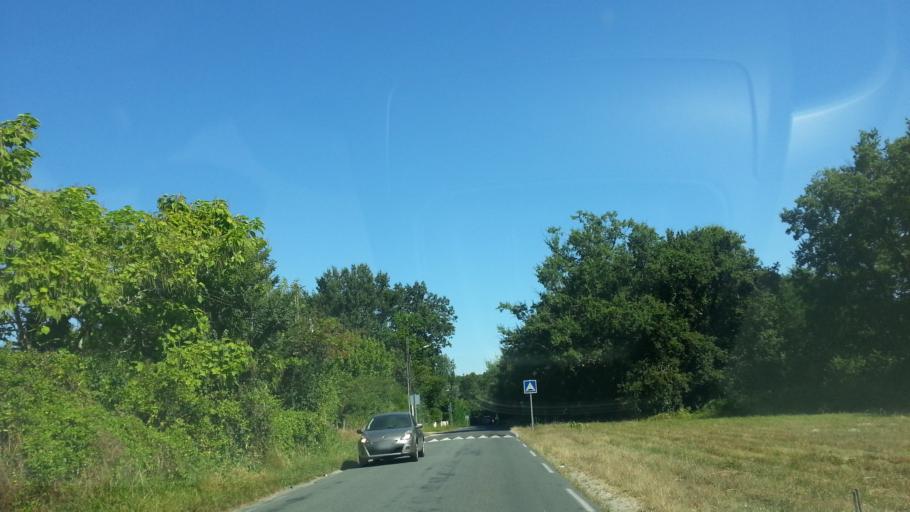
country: FR
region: Aquitaine
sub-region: Departement de la Gironde
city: Saint-Selve
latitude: 44.6865
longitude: -0.5087
